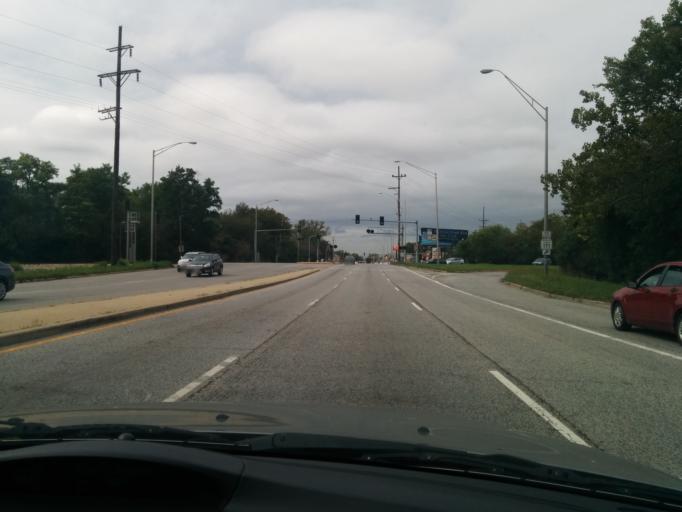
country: US
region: Illinois
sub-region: Cook County
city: North Riverside
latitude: 41.8500
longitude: -87.8279
